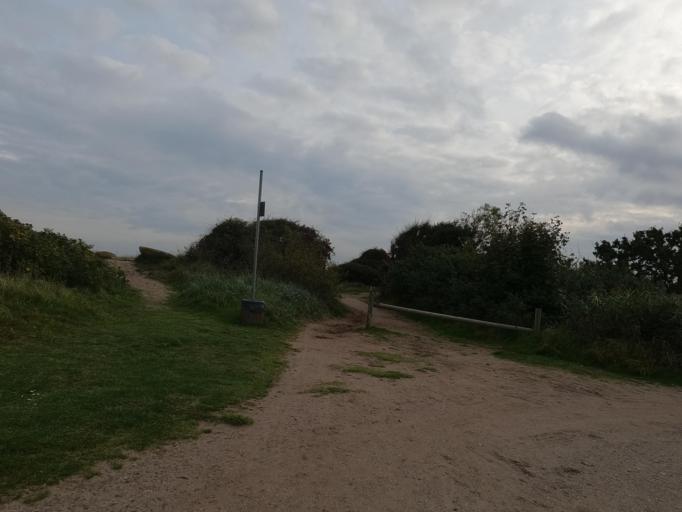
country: DE
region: Schleswig-Holstein
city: Grossenbrode
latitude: 54.3294
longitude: 11.0724
